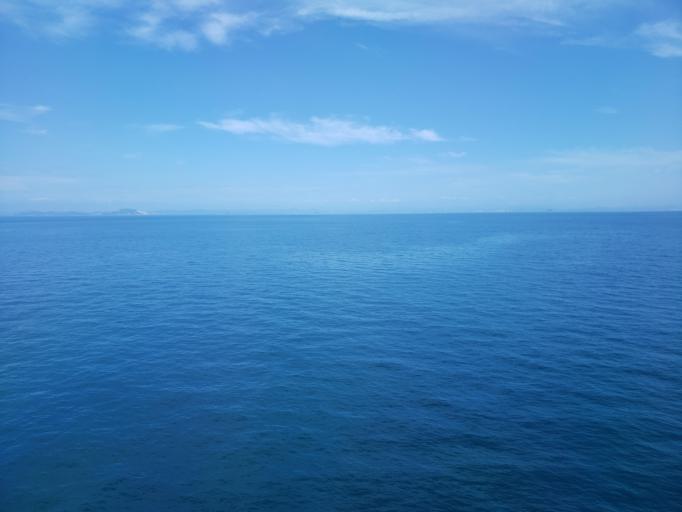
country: JP
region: Hyogo
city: Shirahamacho-usazakiminami
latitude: 34.5423
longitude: 134.7114
